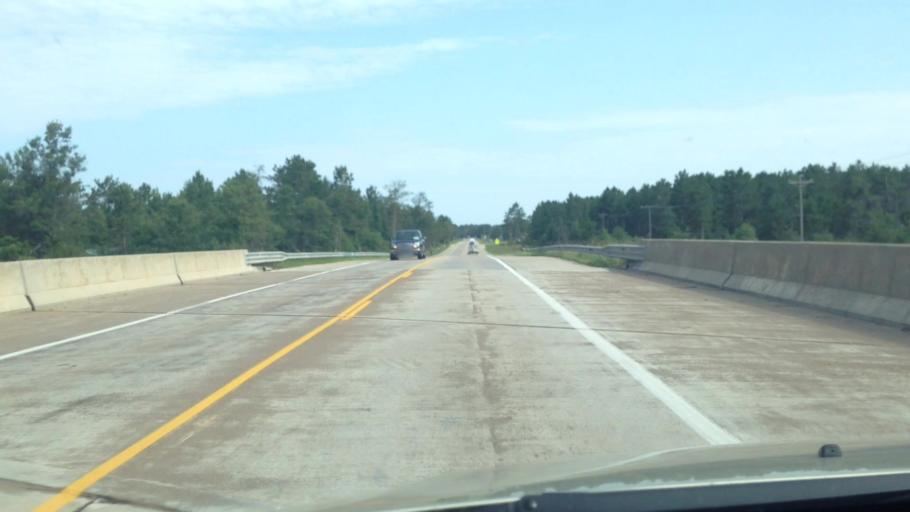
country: US
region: Michigan
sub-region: Delta County
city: Gladstone
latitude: 45.9073
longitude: -86.9294
